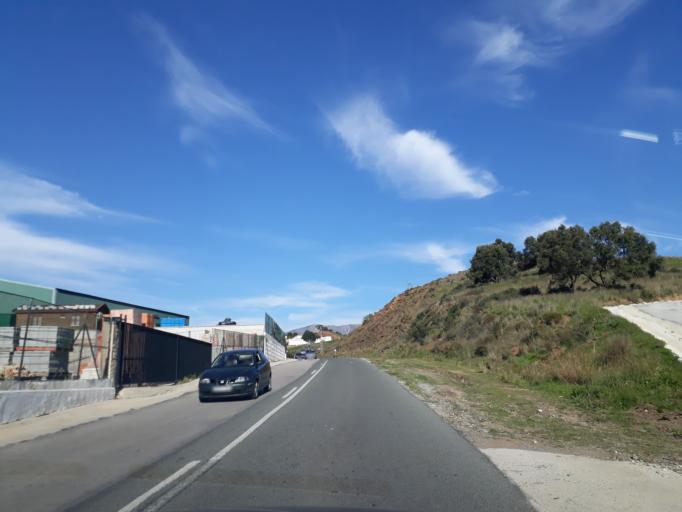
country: ES
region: Andalusia
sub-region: Provincia de Malaga
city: Fuengirola
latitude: 36.5180
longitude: -4.6846
